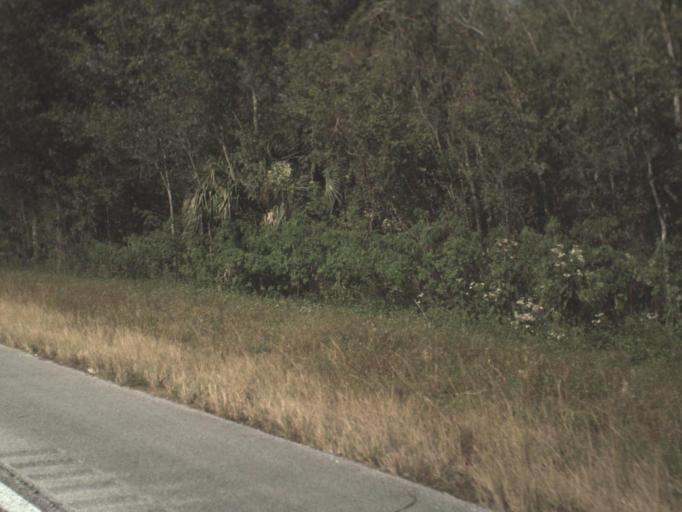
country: US
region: Florida
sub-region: Brevard County
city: Port Saint John
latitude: 28.4337
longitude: -80.8574
